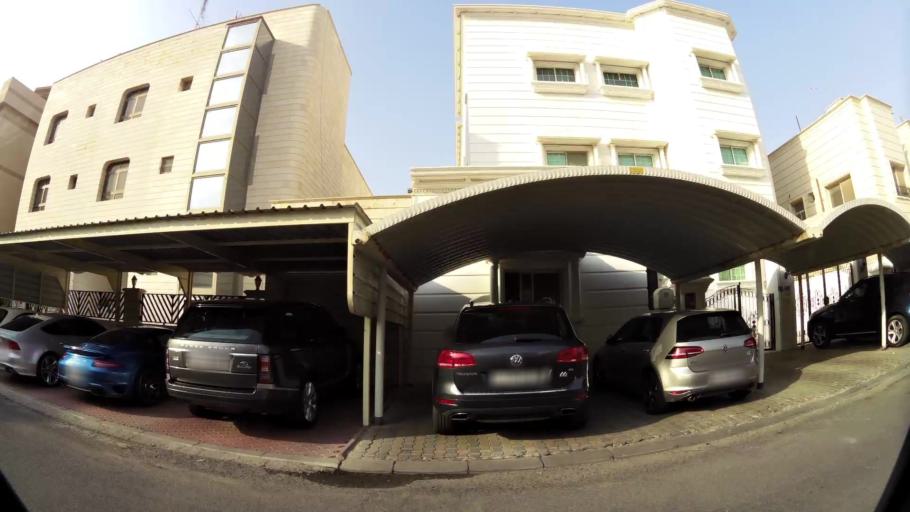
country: KW
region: Muhafazat Hawalli
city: Hawalli
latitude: 29.3206
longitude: 48.0013
